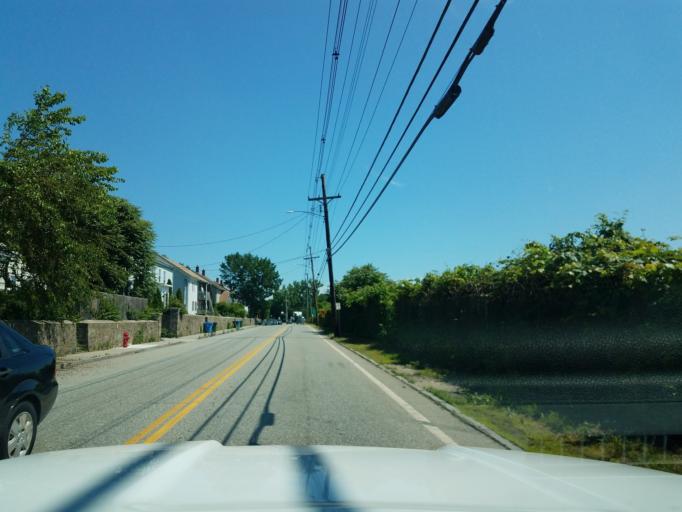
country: US
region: Connecticut
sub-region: New London County
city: Norwich
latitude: 41.5639
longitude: -72.0469
